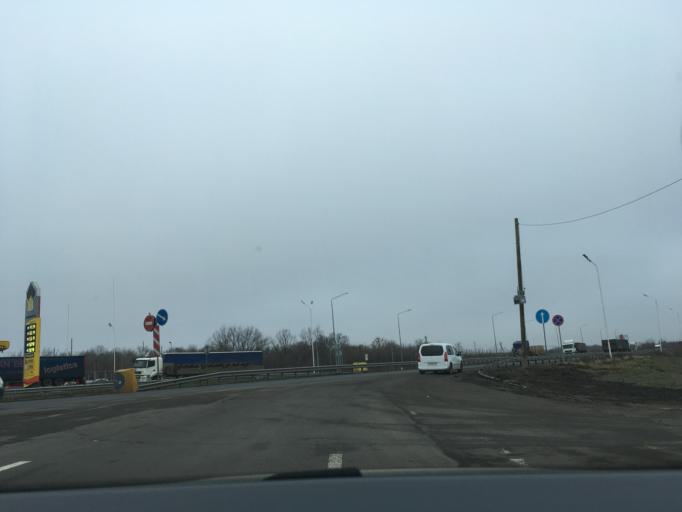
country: RU
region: Rostov
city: Kamensk-Shakhtinskiy
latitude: 48.2760
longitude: 40.2947
